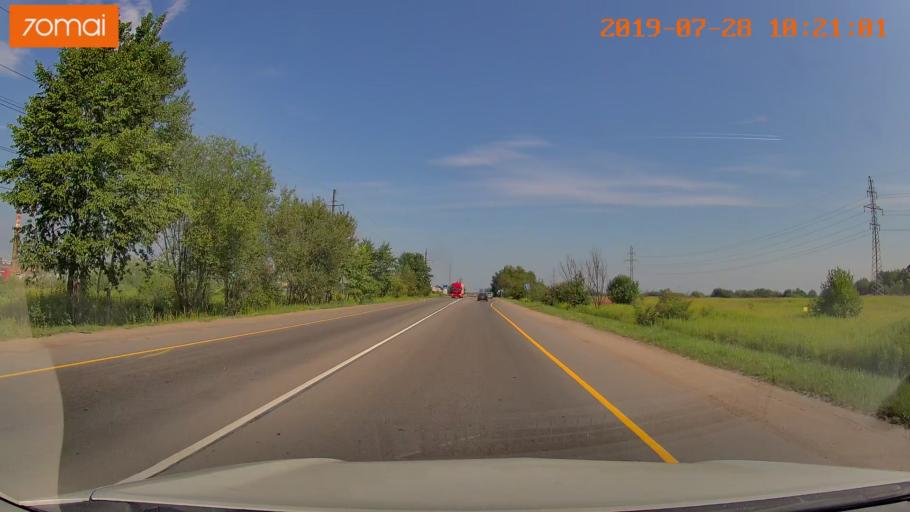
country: RU
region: Kaliningrad
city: Maloye Isakovo
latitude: 54.7534
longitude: 20.5656
